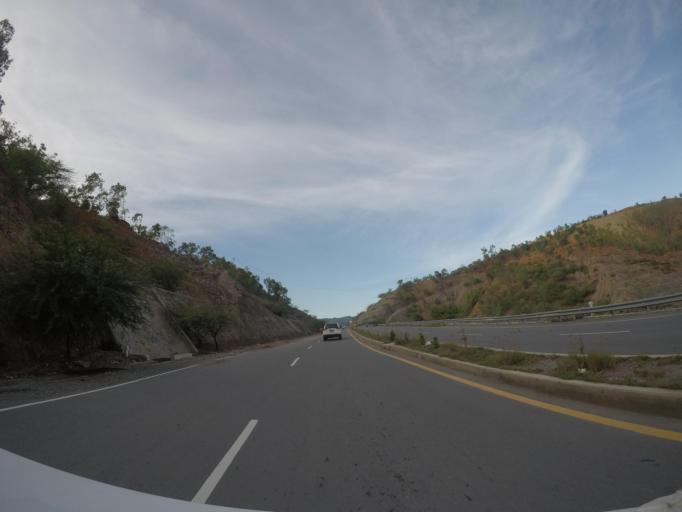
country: TL
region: Dili
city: Dili
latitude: -8.5602
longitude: 125.4943
